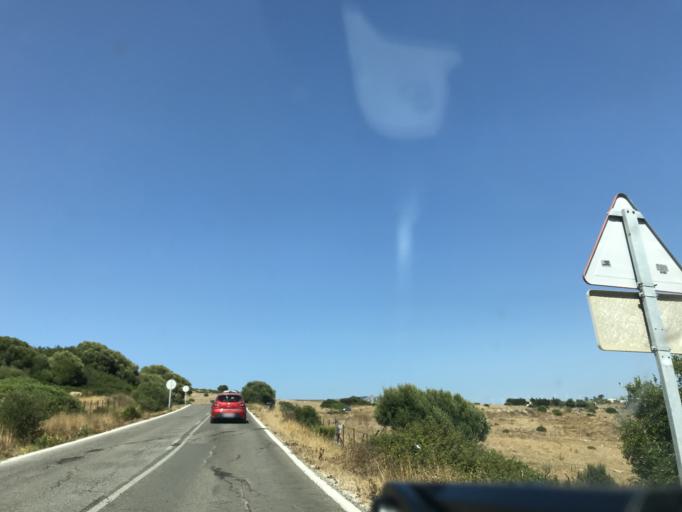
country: ES
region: Andalusia
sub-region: Provincia de Cadiz
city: Zahara de los Atunes
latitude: 36.1024
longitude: -5.7422
